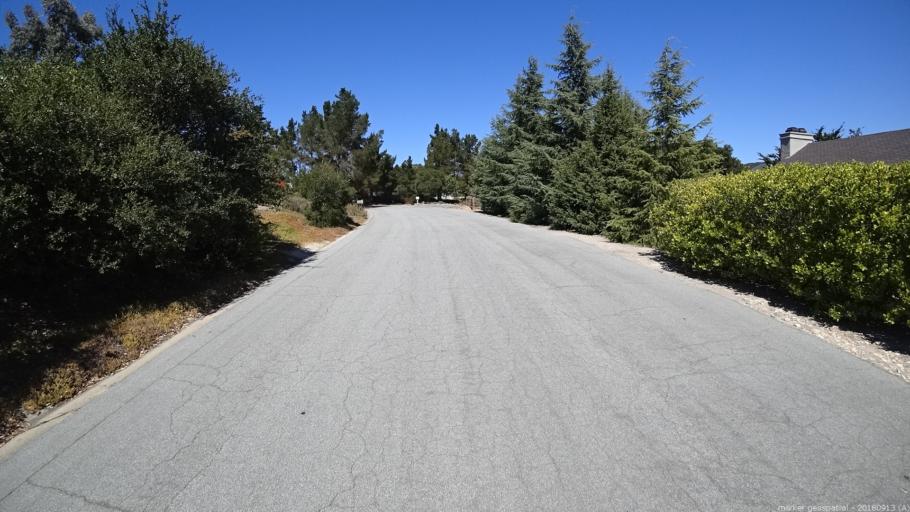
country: US
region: California
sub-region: Monterey County
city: Carmel Valley Village
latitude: 36.5249
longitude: -121.8071
